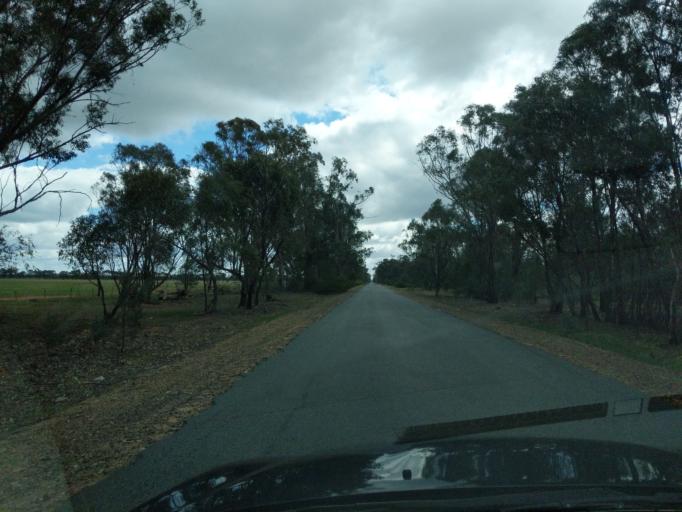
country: AU
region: New South Wales
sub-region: Coolamon
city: Coolamon
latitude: -34.9378
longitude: 146.9693
